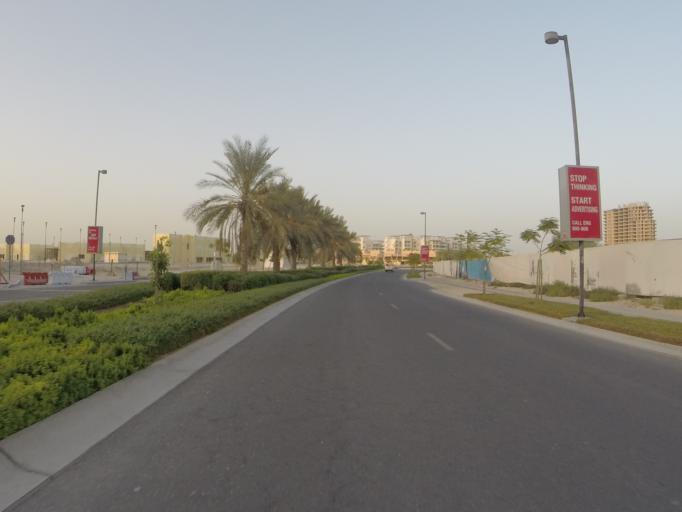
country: AE
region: Dubai
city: Dubai
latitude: 25.0664
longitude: 55.1469
